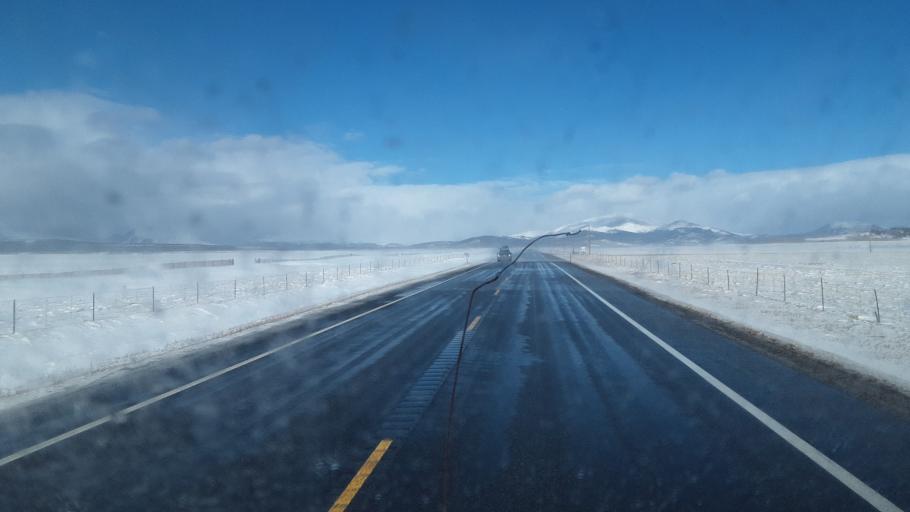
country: US
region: Colorado
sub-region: Park County
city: Fairplay
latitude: 39.1565
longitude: -105.9996
